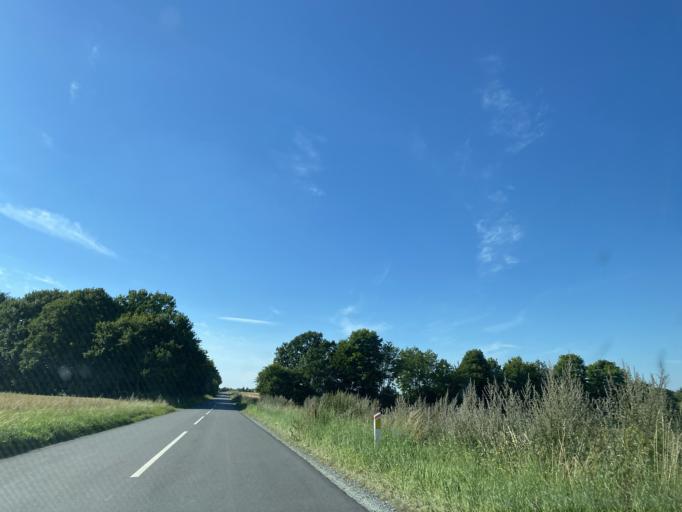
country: DK
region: South Denmark
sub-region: Vejle Kommune
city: Give
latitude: 55.8909
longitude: 9.2923
